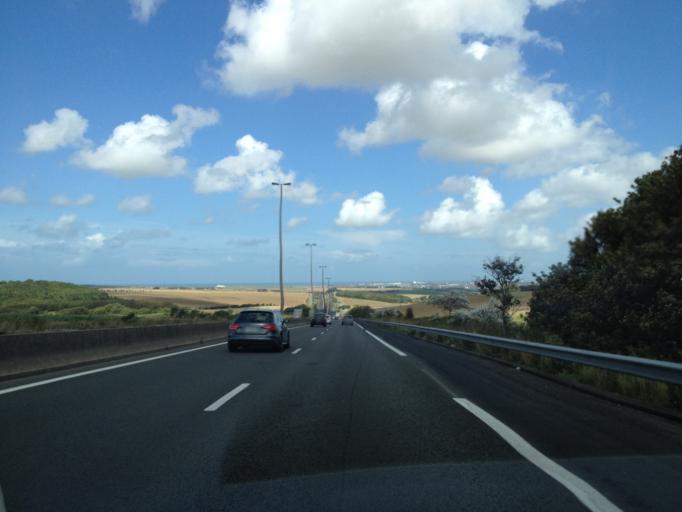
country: FR
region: Nord-Pas-de-Calais
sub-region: Departement du Pas-de-Calais
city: Ferques
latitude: 50.8842
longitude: 1.7531
